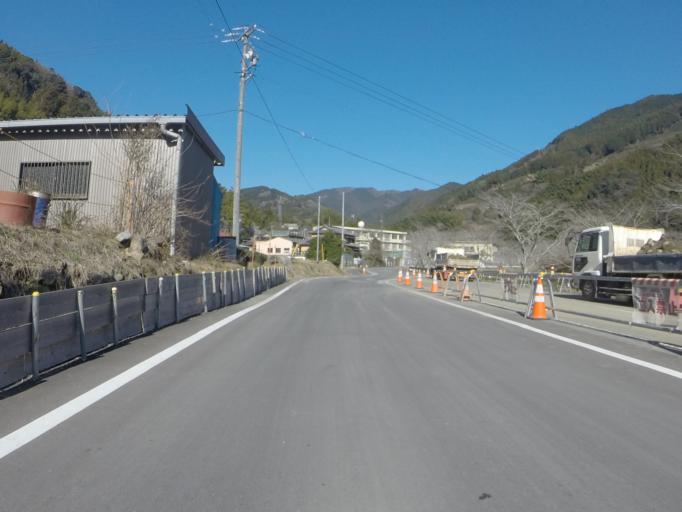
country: JP
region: Shizuoka
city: Fujinomiya
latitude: 35.1353
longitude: 138.4702
